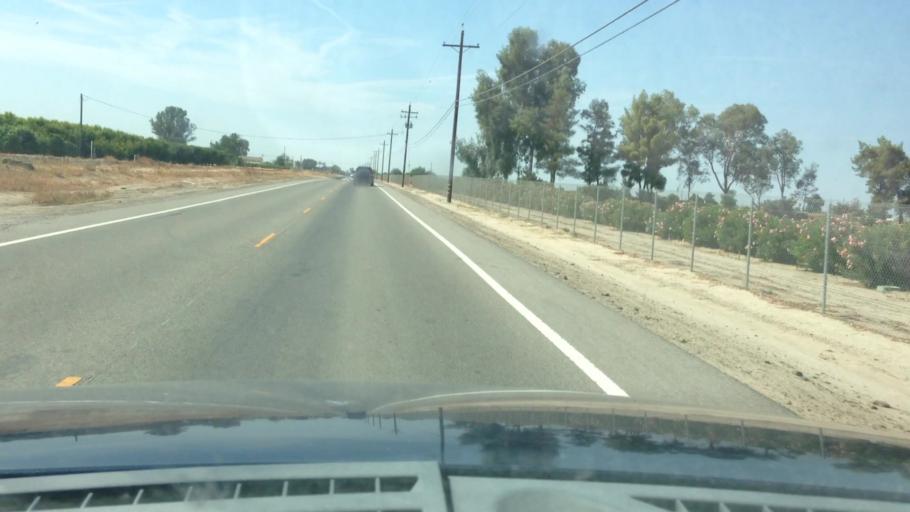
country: US
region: California
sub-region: Fresno County
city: Parlier
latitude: 36.5955
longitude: -119.5570
